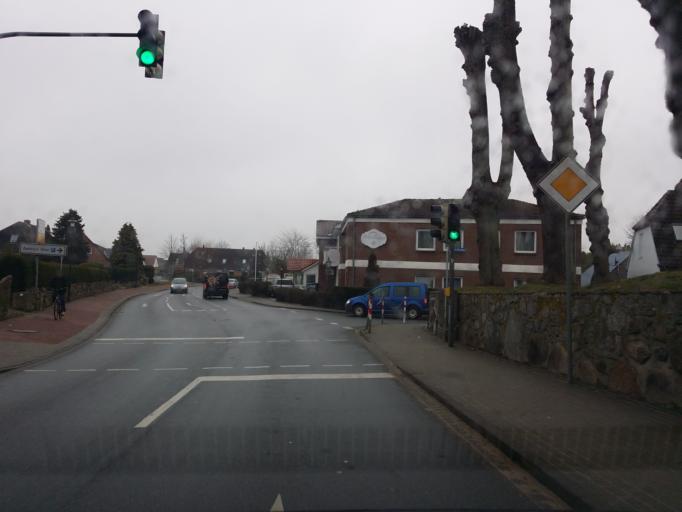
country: DE
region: Schleswig-Holstein
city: Fehmarn
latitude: 54.4357
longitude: 11.1951
